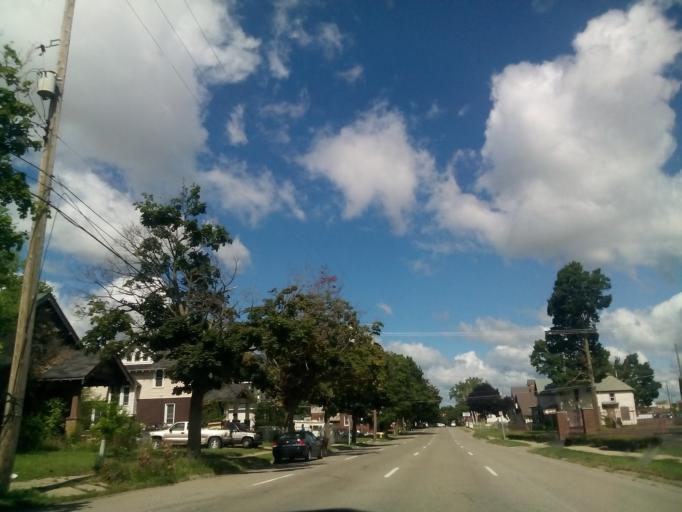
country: US
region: Michigan
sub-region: Genesee County
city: Flint
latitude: 43.0079
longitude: -83.6868
